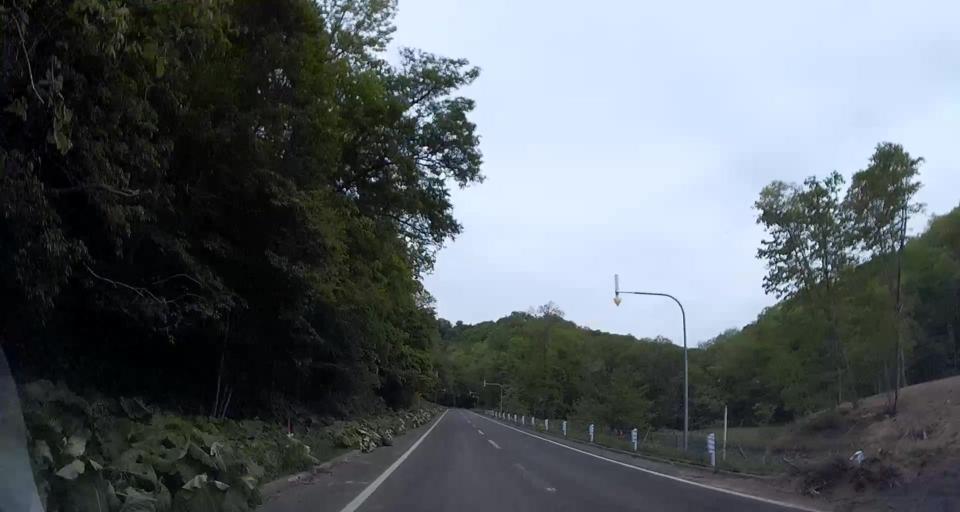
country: JP
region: Hokkaido
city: Chitose
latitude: 42.7909
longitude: 142.0529
